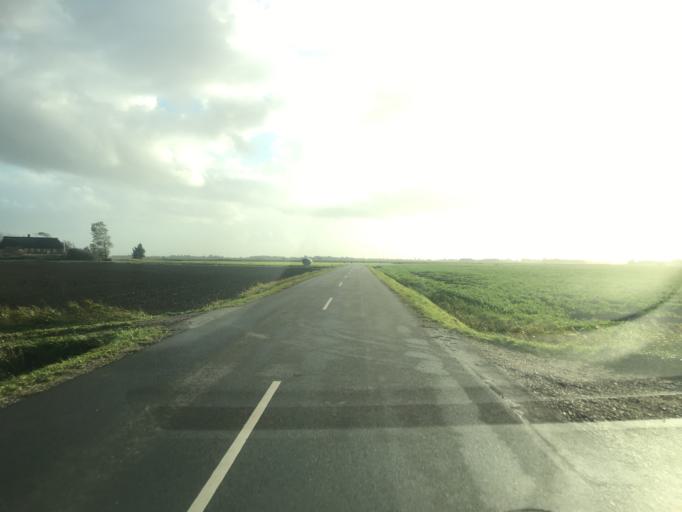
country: DE
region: Schleswig-Holstein
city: Aventoft
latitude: 54.9179
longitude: 8.7853
